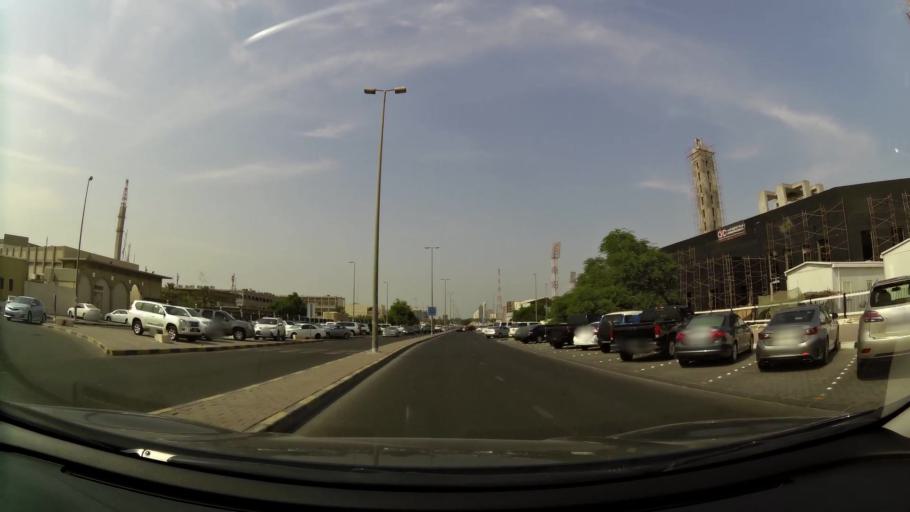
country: KW
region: Al Asimah
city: Ash Shamiyah
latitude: 29.3395
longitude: 47.9531
